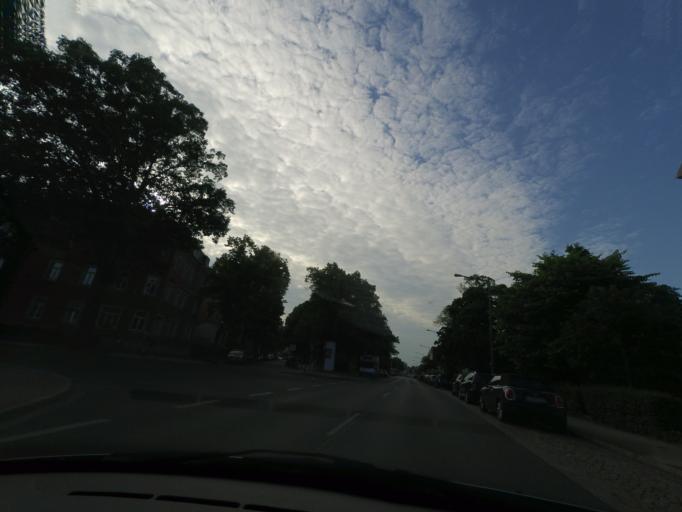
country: DE
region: Saxony
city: Heidenau
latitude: 51.0216
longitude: 13.8402
